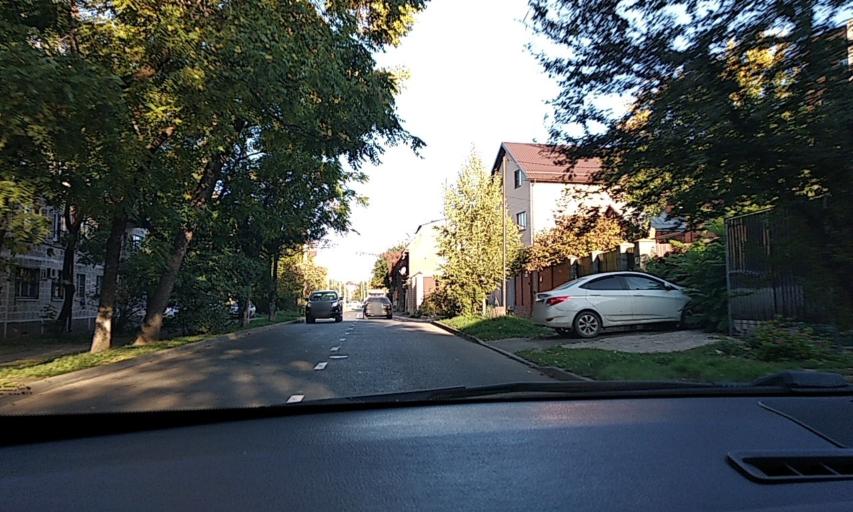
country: RU
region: Adygeya
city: Yablonovskiy
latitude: 45.0109
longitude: 38.9621
